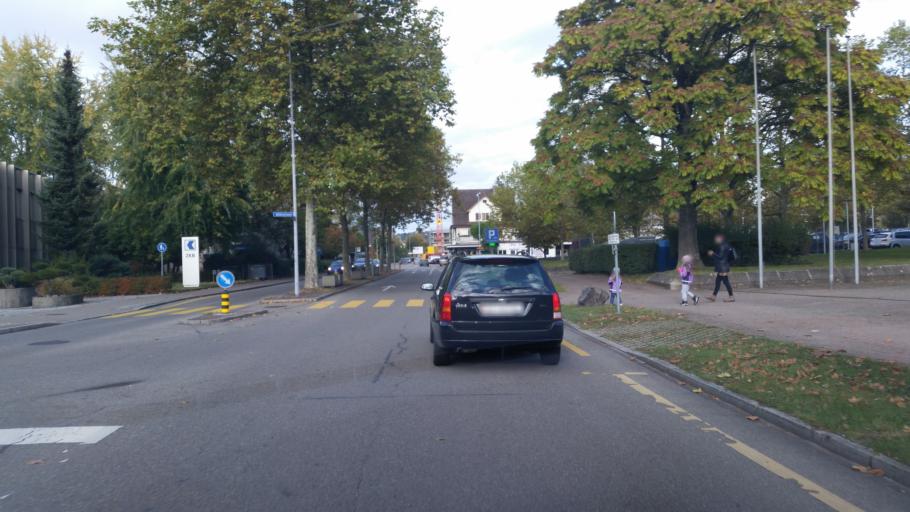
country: CH
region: Zurich
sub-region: Bezirk Dielsdorf
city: Regensdorf
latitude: 47.4319
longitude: 8.4667
